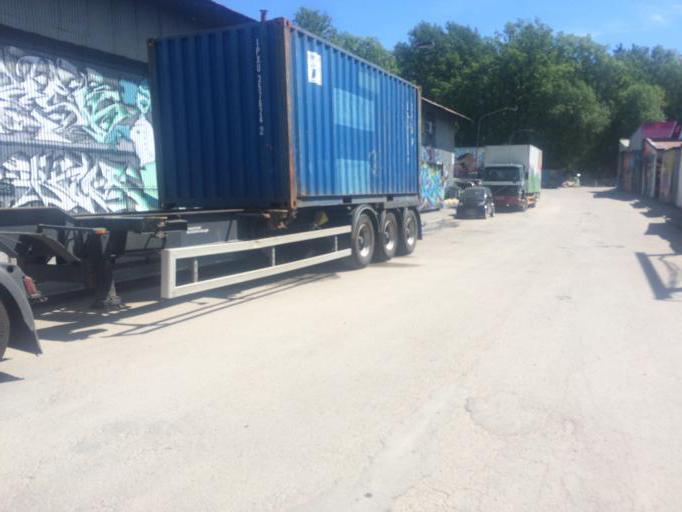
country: SE
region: Stockholm
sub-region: Stockholms Kommun
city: Arsta
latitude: 59.2484
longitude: 18.0432
